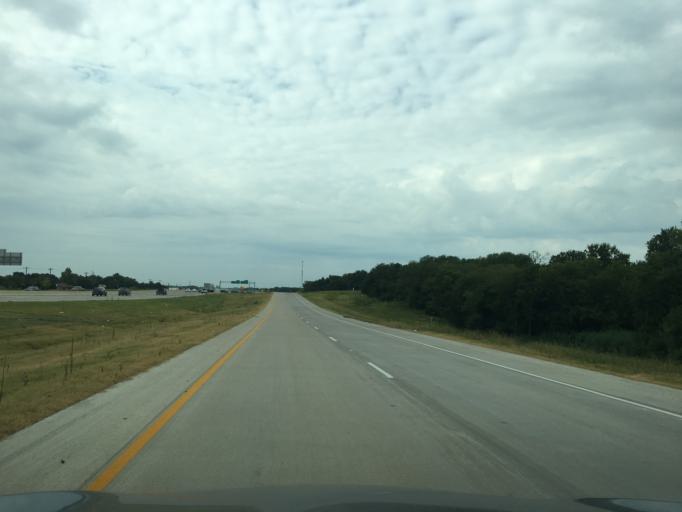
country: US
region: Texas
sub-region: Collin County
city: Anna
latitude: 33.3321
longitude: -96.5894
